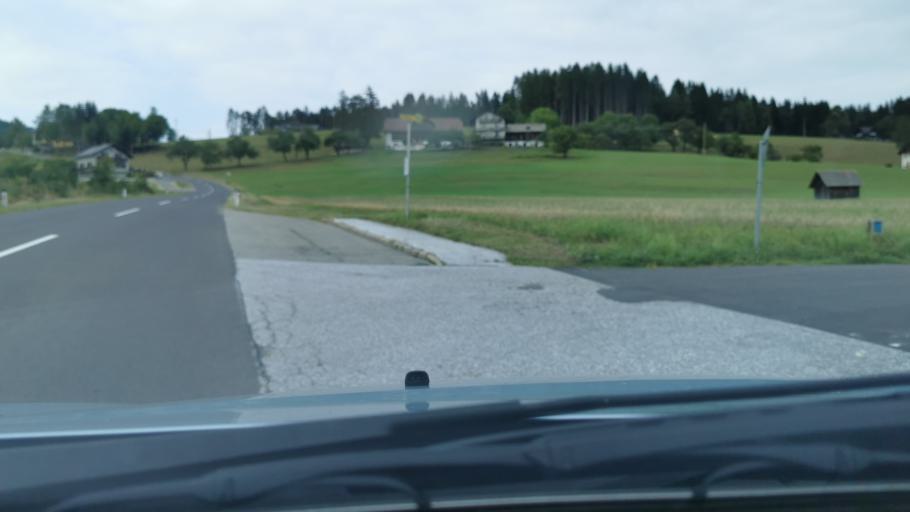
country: AT
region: Styria
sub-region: Politischer Bezirk Weiz
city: Fischbach
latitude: 47.3938
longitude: 15.6687
